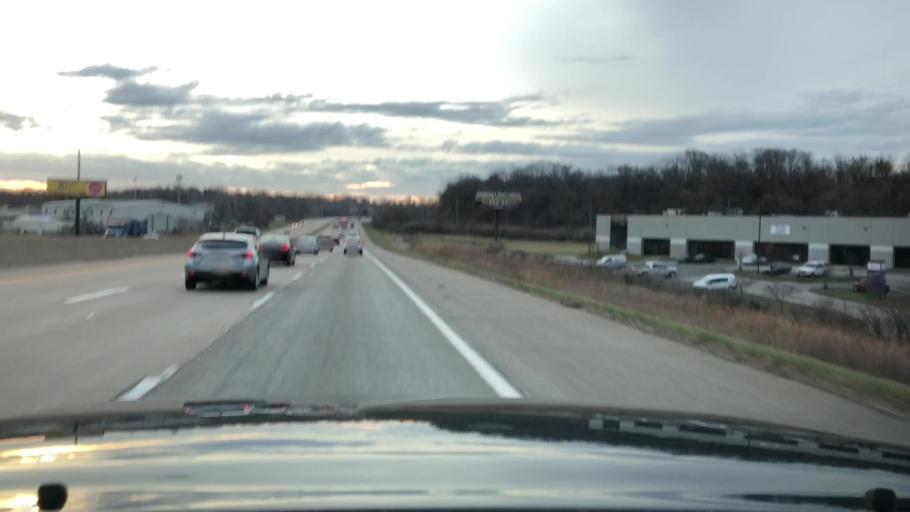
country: US
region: Missouri
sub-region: Saint Charles County
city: Saint Charles
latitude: 38.8206
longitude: -90.5054
